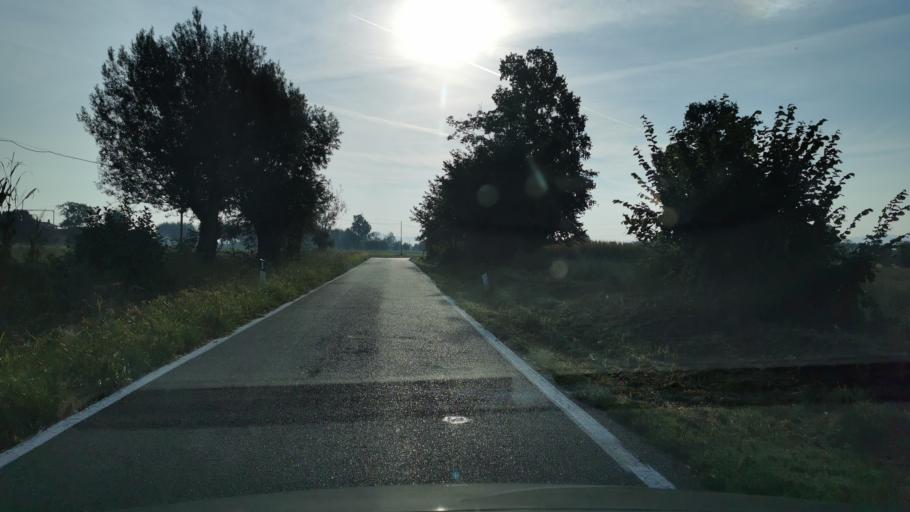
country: IT
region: Piedmont
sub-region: Provincia di Torino
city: Borgaro Torinese
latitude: 45.1623
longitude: 7.6756
